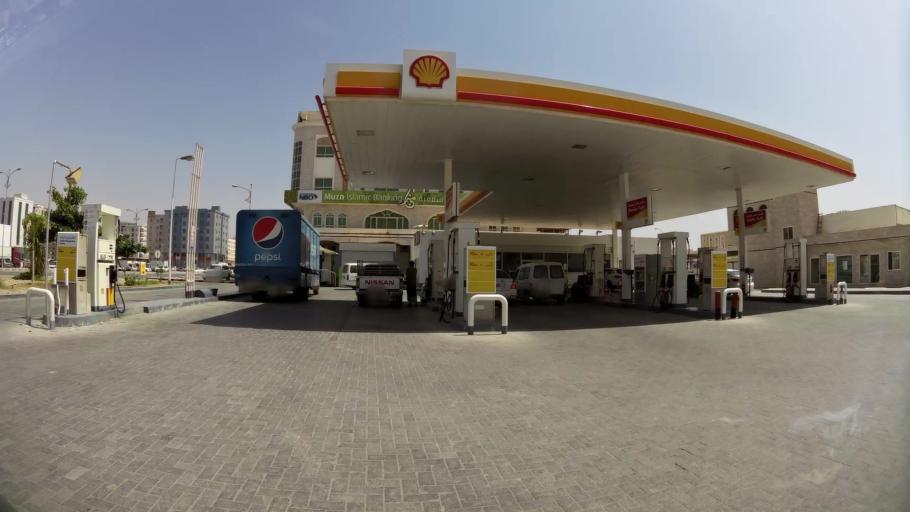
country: OM
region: Zufar
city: Salalah
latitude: 17.0186
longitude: 54.1011
